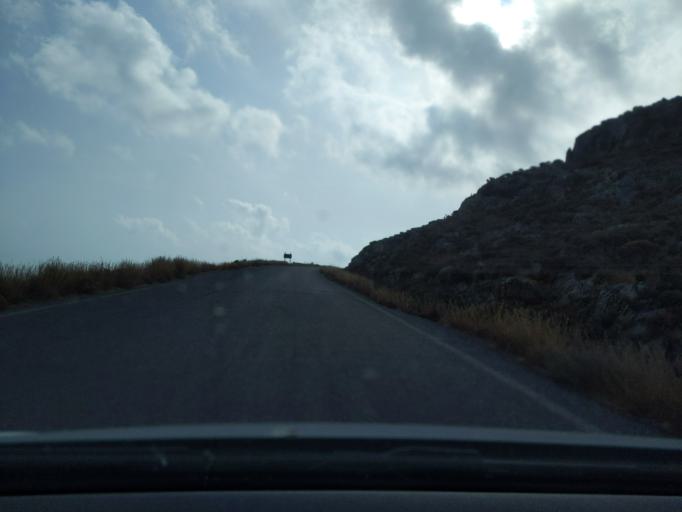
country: GR
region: Crete
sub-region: Nomos Lasithiou
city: Palekastro
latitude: 35.0936
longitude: 26.2614
